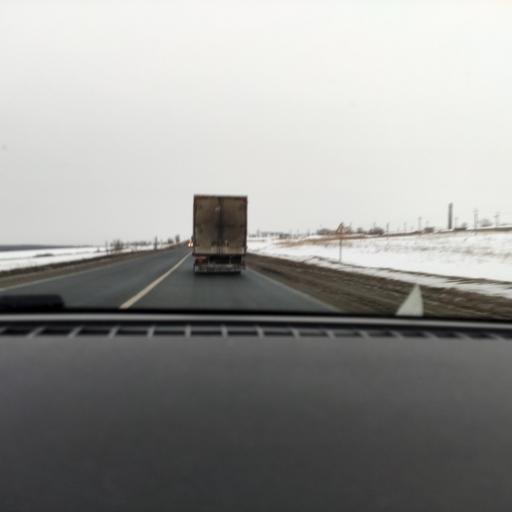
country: RU
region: Samara
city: Smyshlyayevka
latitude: 53.3011
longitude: 50.4587
